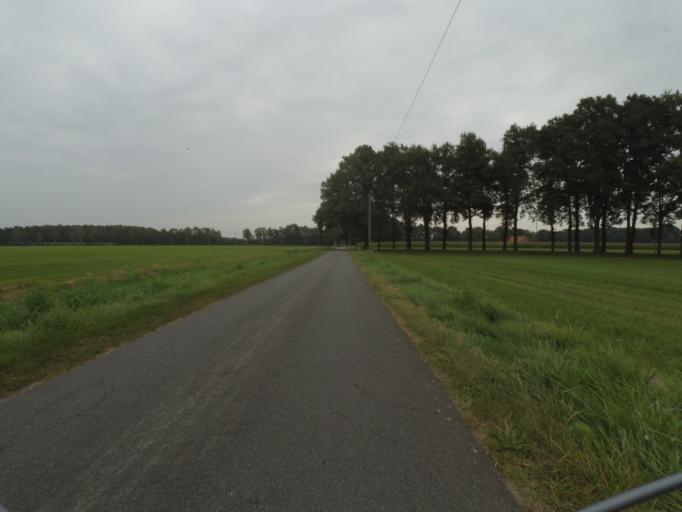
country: NL
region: Overijssel
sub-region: Gemeente Losser
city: Losser
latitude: 52.2760
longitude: 7.0593
